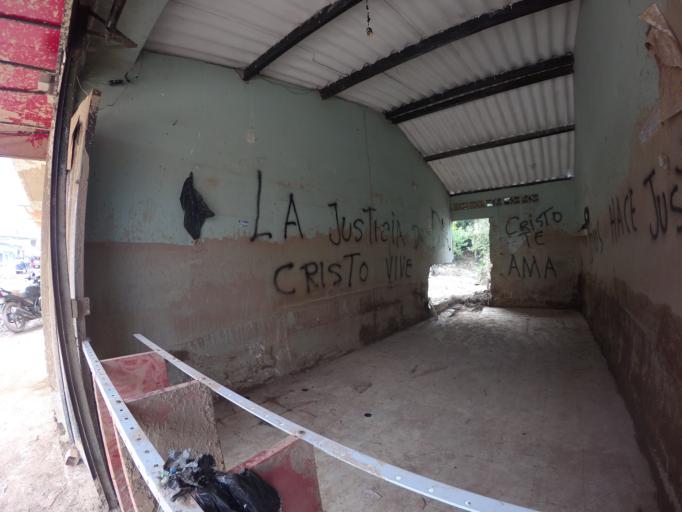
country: CO
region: Putumayo
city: Mocoa
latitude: 1.1497
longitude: -76.6490
